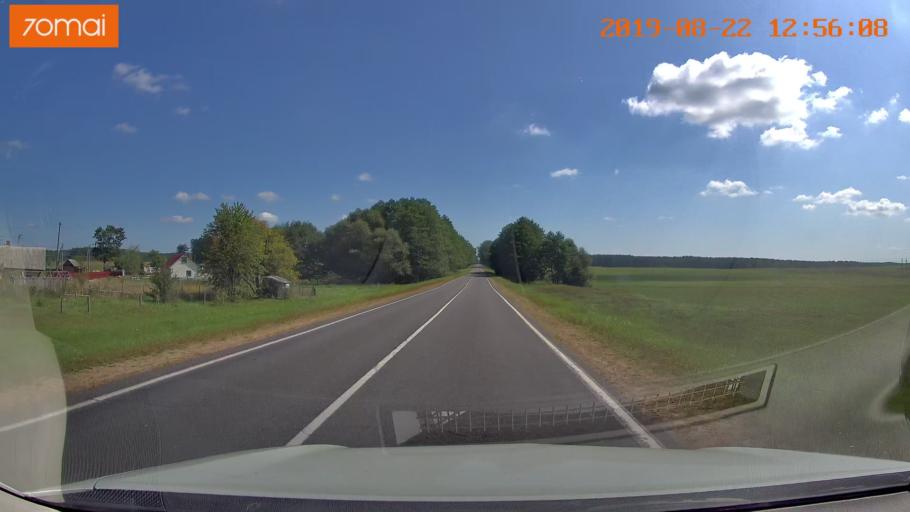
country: BY
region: Minsk
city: Prawdzinski
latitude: 53.4341
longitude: 27.7257
